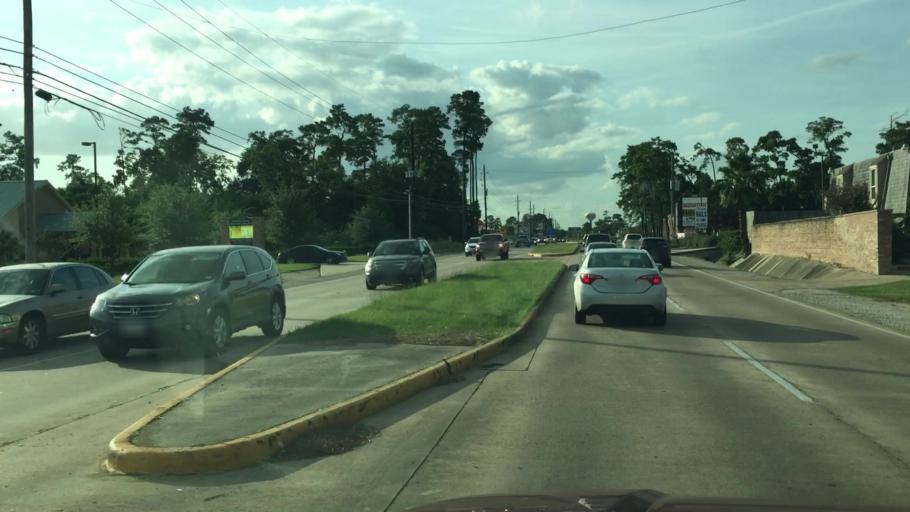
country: US
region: Texas
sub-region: Harris County
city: Hudson
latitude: 30.0126
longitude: -95.5163
